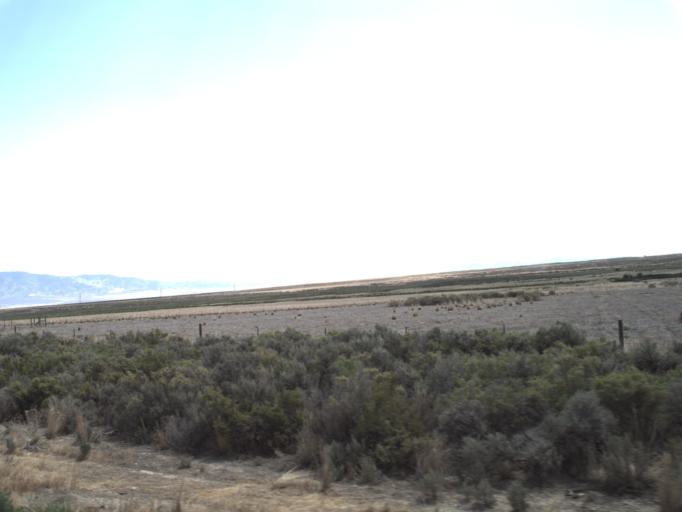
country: US
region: Utah
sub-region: Tooele County
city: Tooele
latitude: 40.1865
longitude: -112.4198
